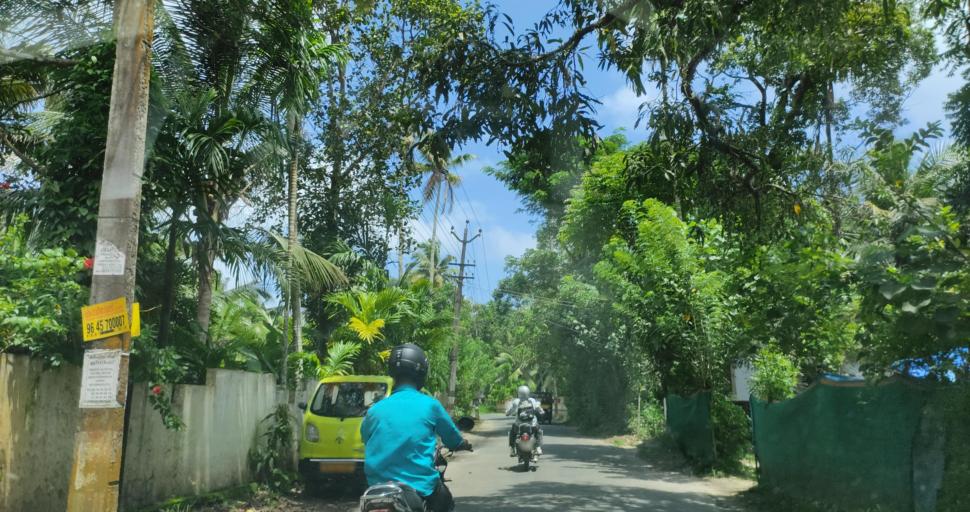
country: IN
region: Kerala
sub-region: Alappuzha
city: Vayalar
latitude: 9.7066
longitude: 76.3389
